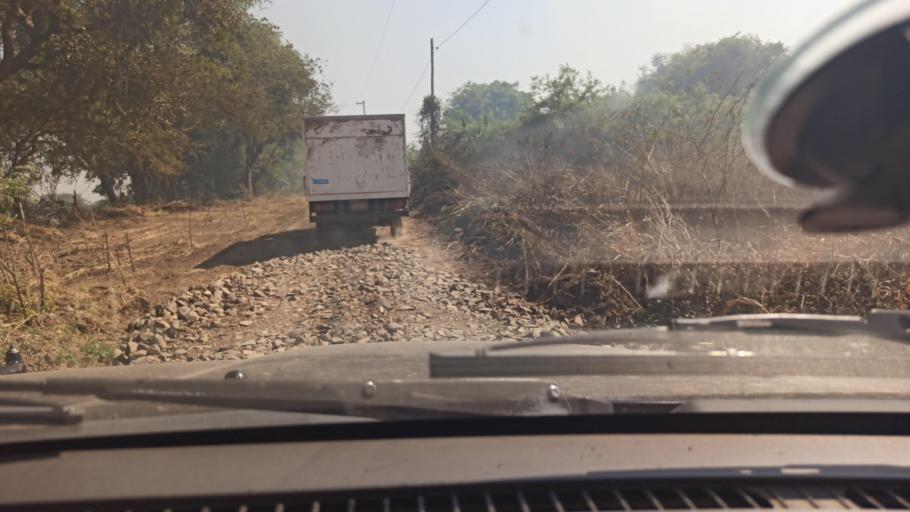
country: PY
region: Asuncion
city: Asuncion
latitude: -25.3462
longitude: -57.6728
